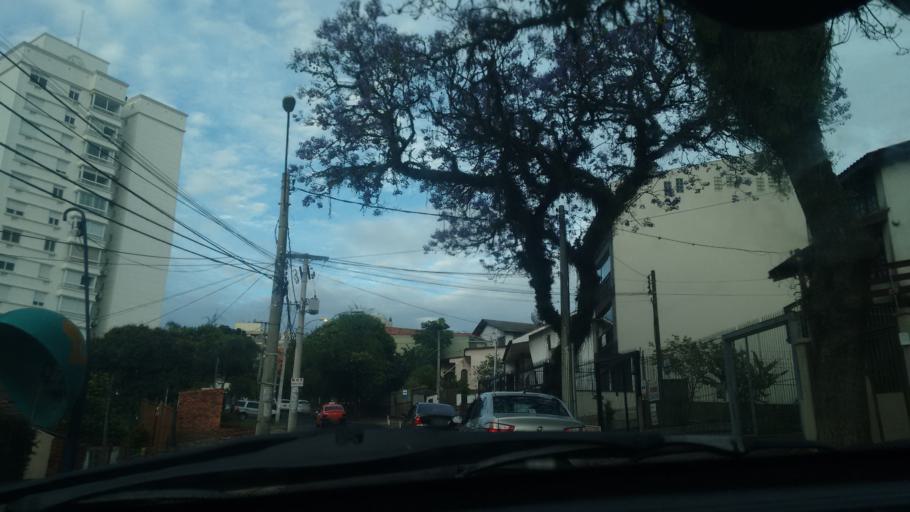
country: BR
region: Rio Grande do Sul
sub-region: Porto Alegre
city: Porto Alegre
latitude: -30.0081
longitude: -51.1555
